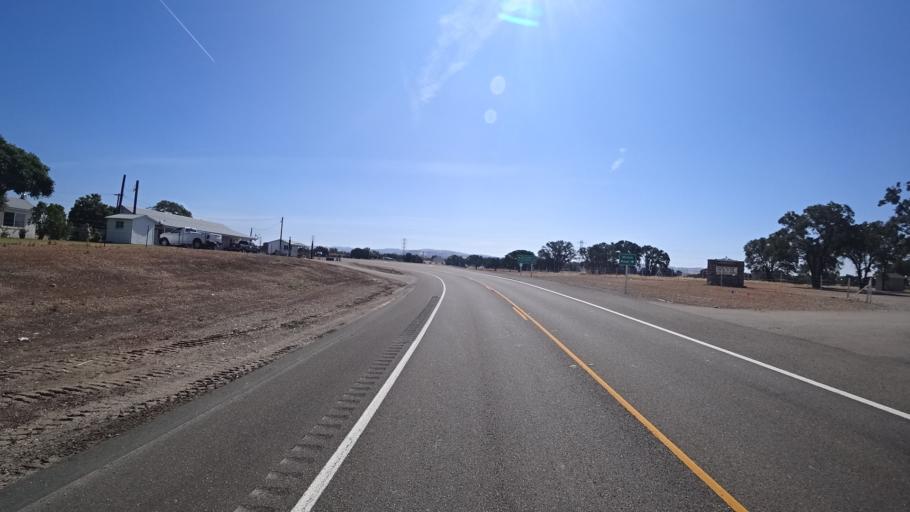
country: US
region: California
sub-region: Calaveras County
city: Rancho Calaveras
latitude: 38.1049
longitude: -120.9114
